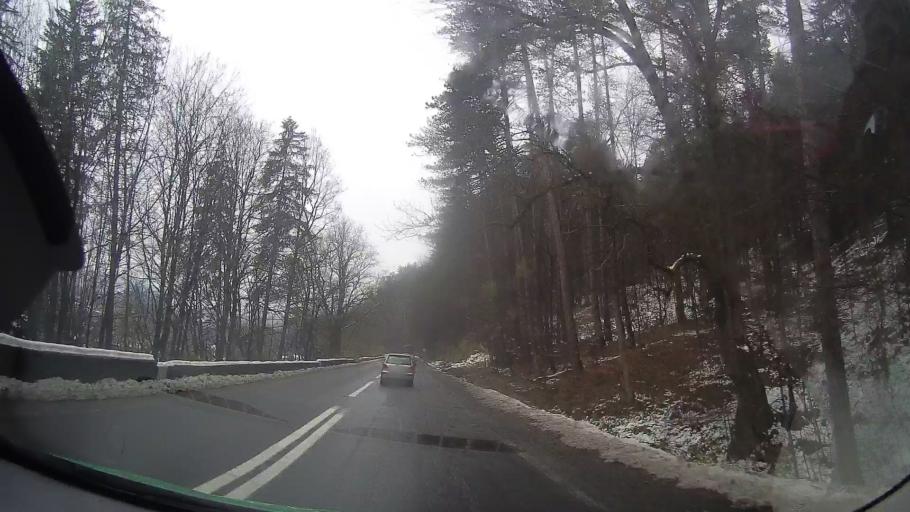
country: RO
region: Neamt
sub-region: Comuna Tarcau
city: Tarcau
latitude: 46.8962
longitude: 26.1225
